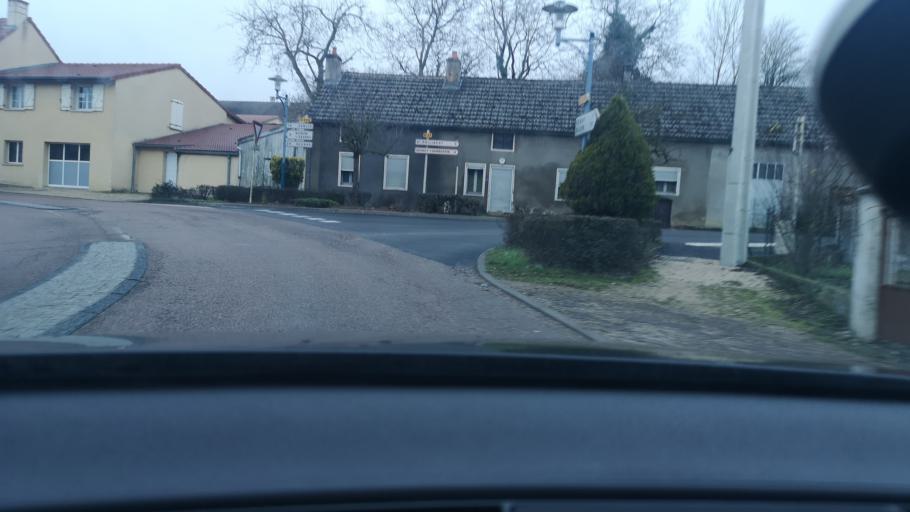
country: FR
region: Bourgogne
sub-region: Departement de la Cote-d'Or
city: Fenay
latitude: 47.2236
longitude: 5.0617
